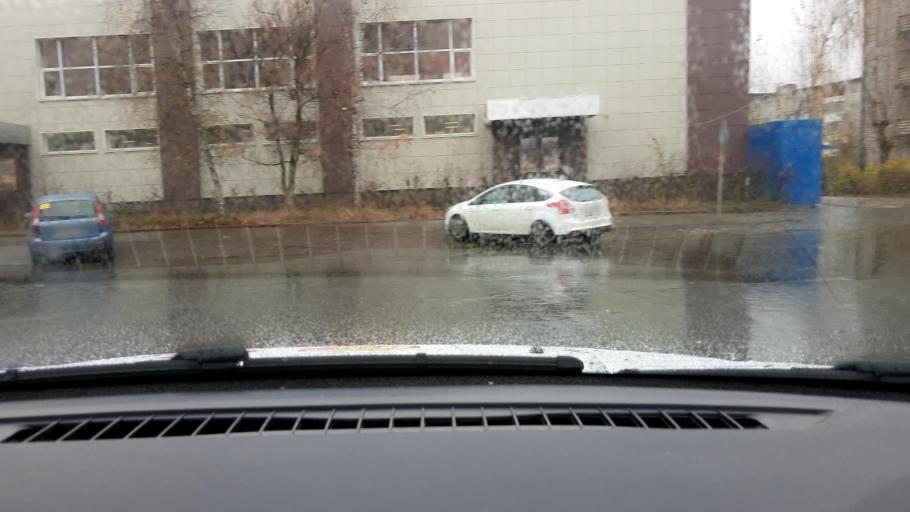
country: RU
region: Nizjnij Novgorod
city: Dzerzhinsk
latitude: 56.2366
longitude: 43.4428
